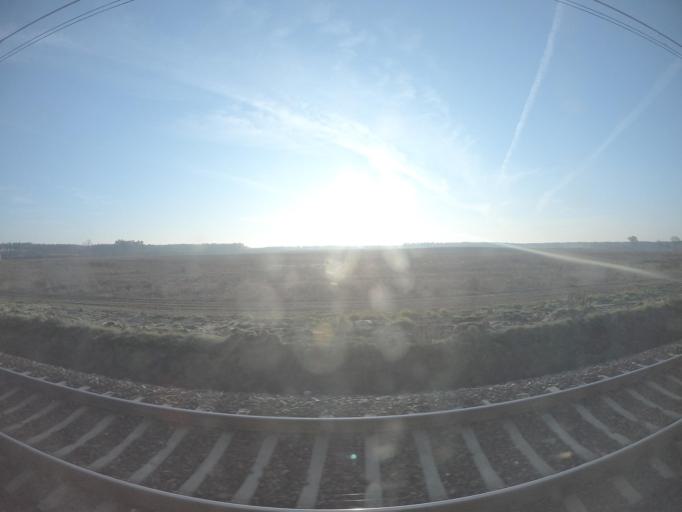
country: PL
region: Lubusz
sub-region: Powiat slubicki
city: Rzepin
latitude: 52.2921
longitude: 14.8862
